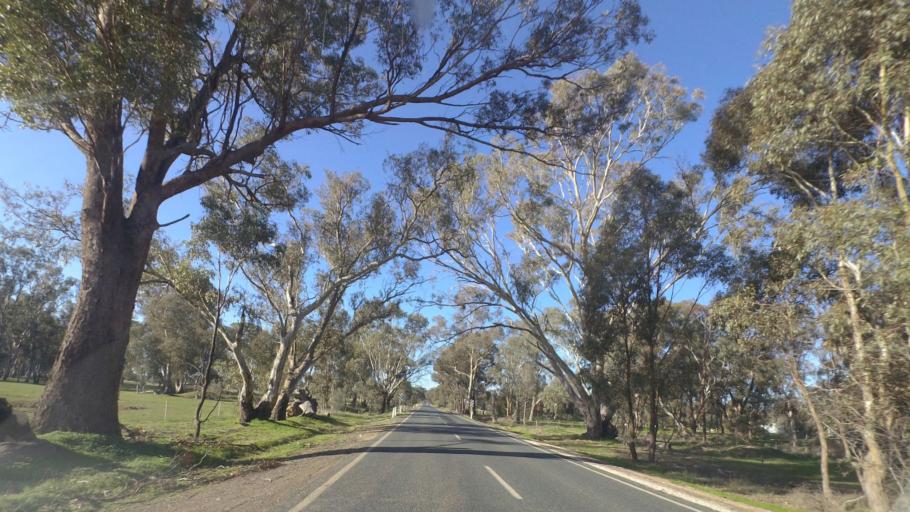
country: AU
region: Victoria
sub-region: Greater Bendigo
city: Epsom
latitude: -36.6756
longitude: 144.3943
